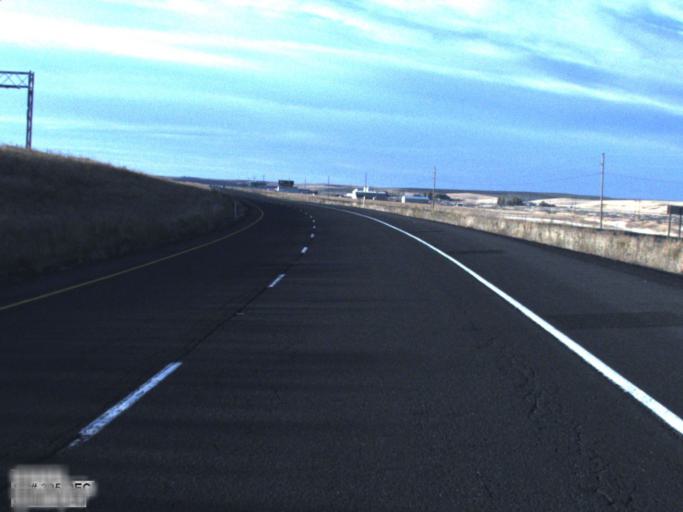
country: US
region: Washington
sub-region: Adams County
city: Ritzville
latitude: 47.1023
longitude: -118.4081
